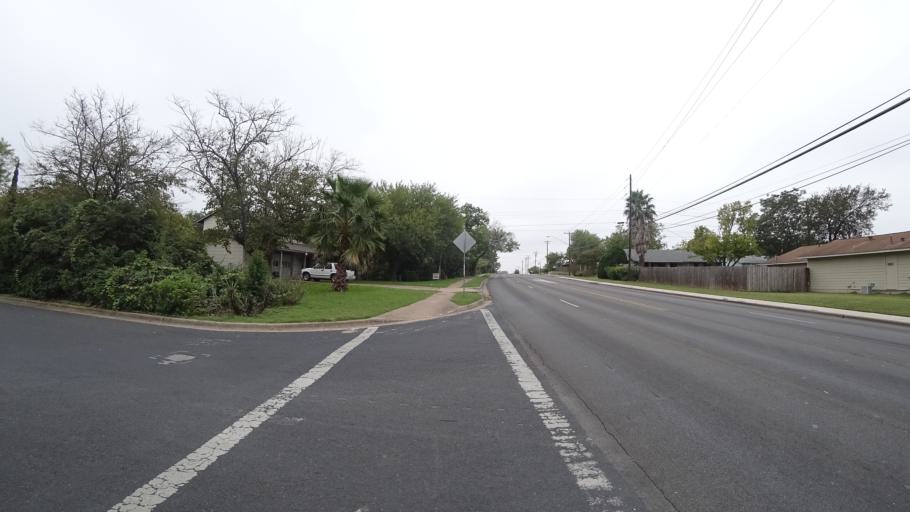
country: US
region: Texas
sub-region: Travis County
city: Austin
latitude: 30.2112
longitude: -97.7792
